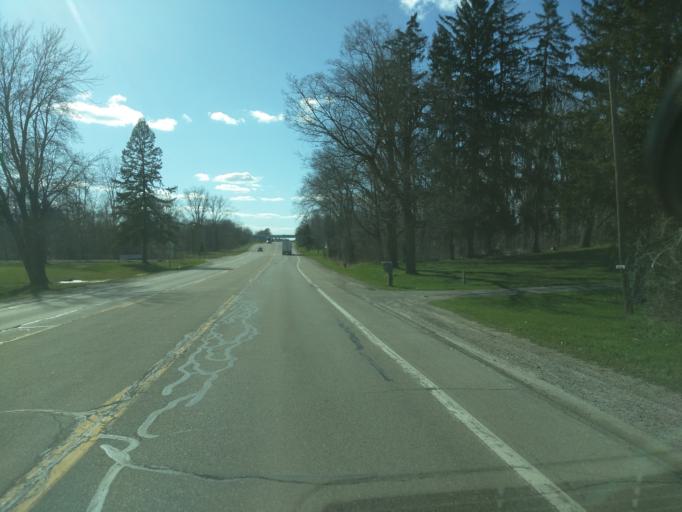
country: US
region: Michigan
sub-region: Eaton County
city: Waverly
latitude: 42.7826
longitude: -84.6577
